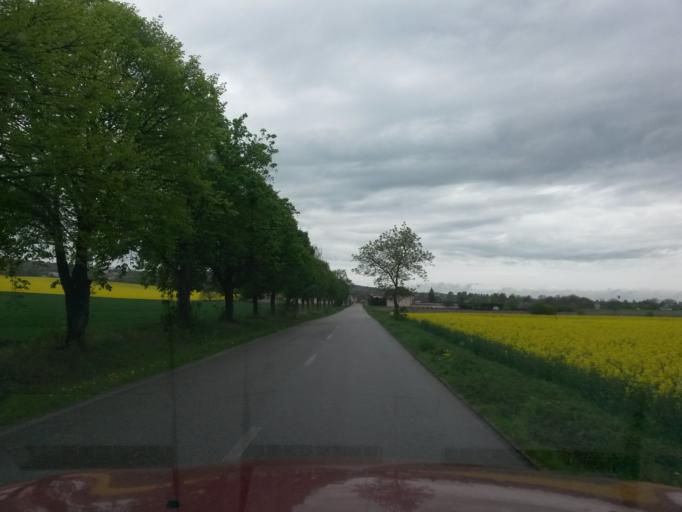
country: HU
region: Borsod-Abauj-Zemplen
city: Gonc
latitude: 48.5380
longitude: 21.1985
